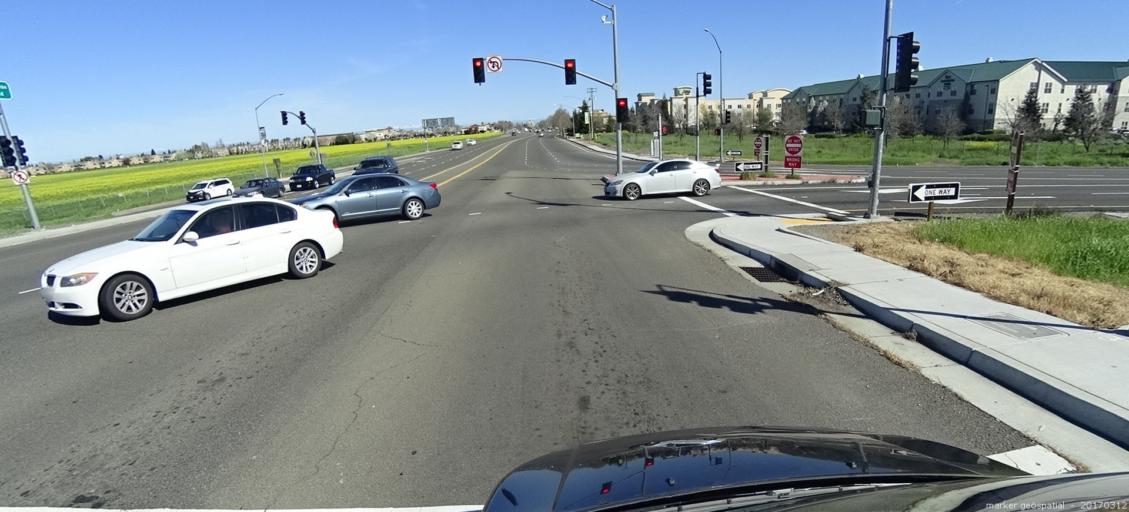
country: US
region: California
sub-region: Yolo County
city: West Sacramento
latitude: 38.6558
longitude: -121.5314
